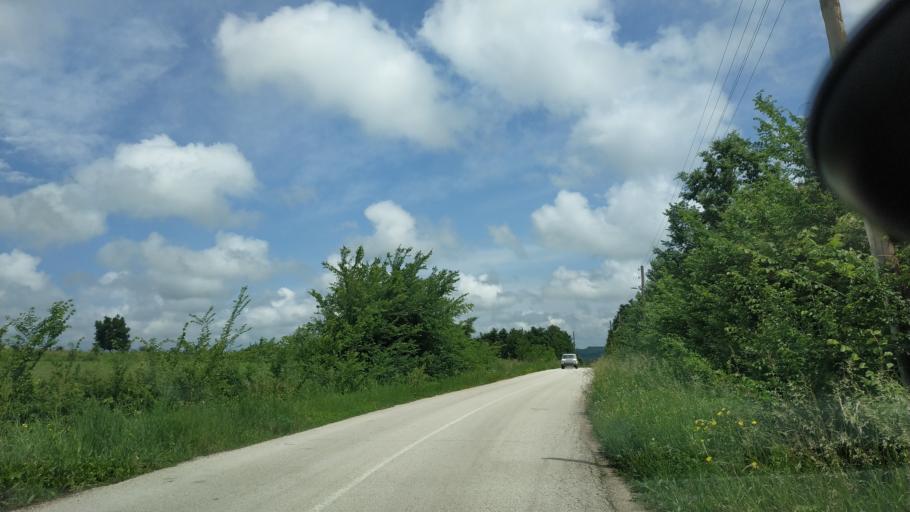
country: RS
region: Central Serbia
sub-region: Zajecarski Okrug
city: Boljevac
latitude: 43.8181
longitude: 21.9519
